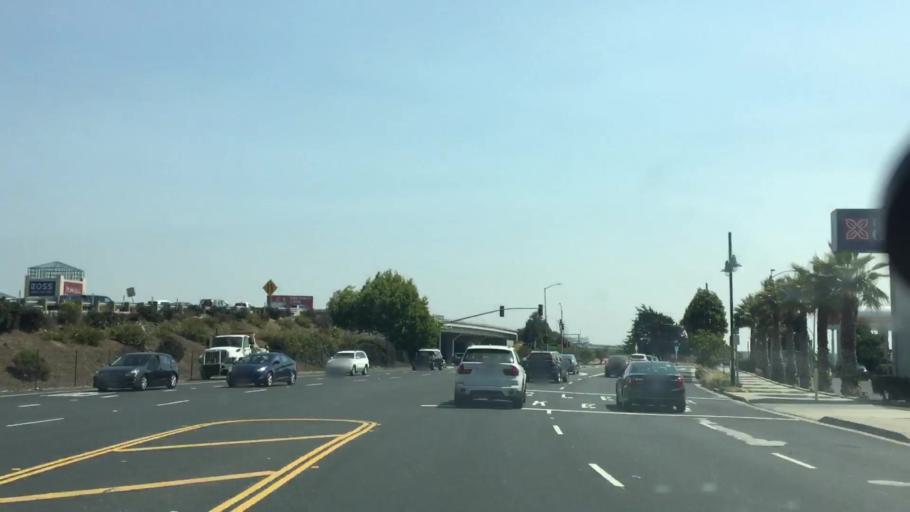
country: US
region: California
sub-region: Alameda County
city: Emeryville
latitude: 37.8392
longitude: -122.2977
